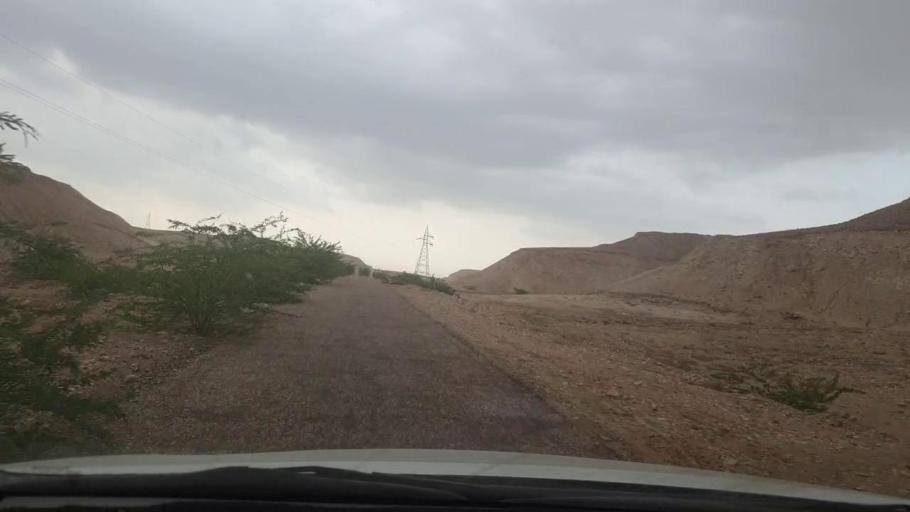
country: PK
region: Sindh
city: Khairpur
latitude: 27.4657
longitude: 68.9234
